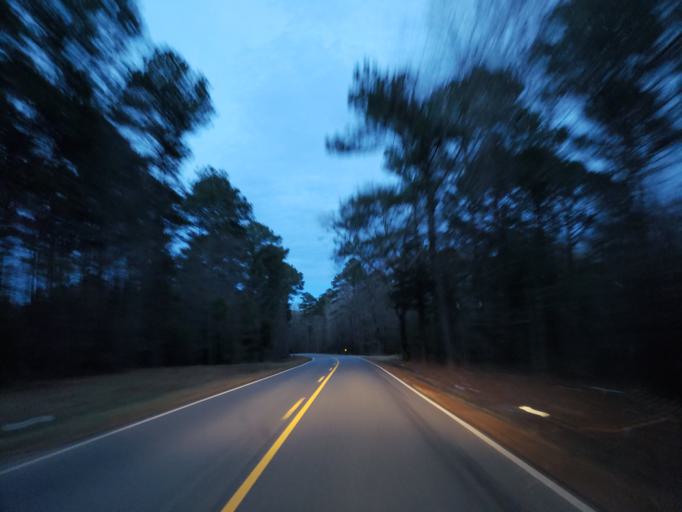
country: US
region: Alabama
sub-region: Greene County
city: Eutaw
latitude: 32.8964
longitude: -88.0321
